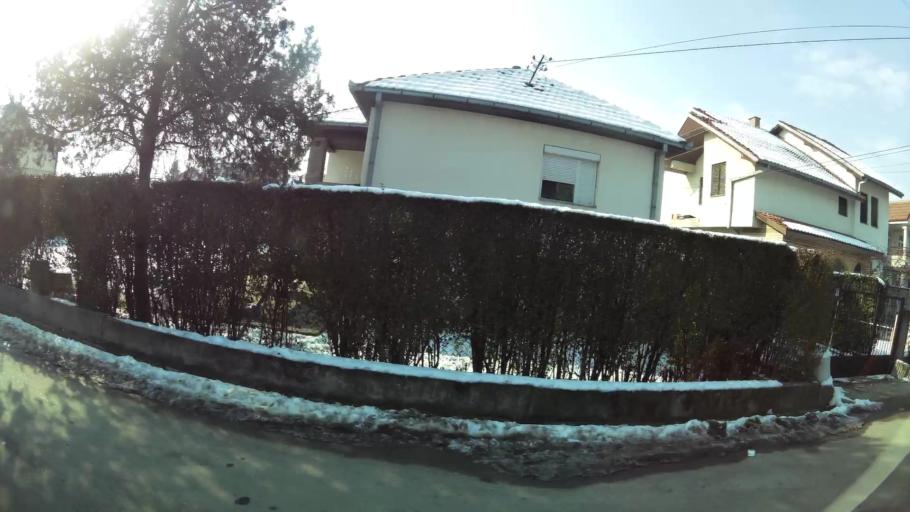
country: MK
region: Suto Orizari
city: Suto Orizare
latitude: 42.0264
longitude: 21.3770
